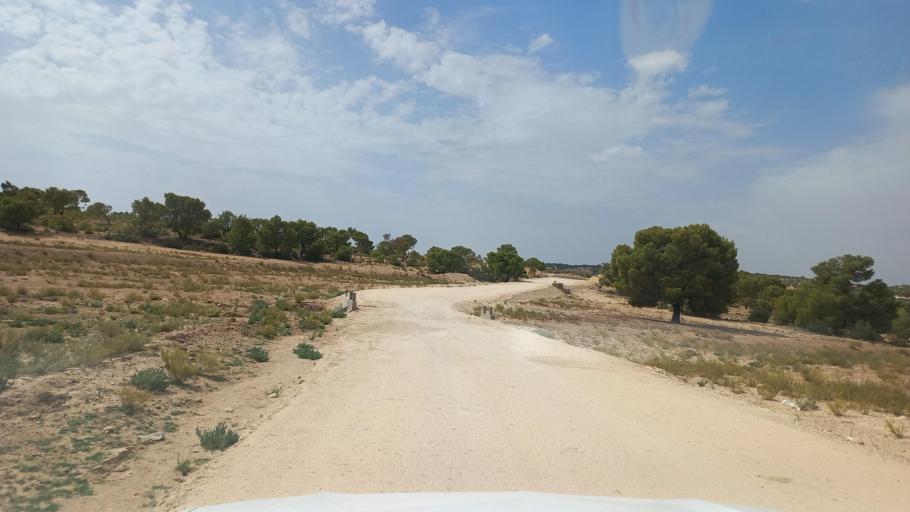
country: TN
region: Al Qasrayn
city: Kasserine
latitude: 35.3839
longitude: 8.8694
